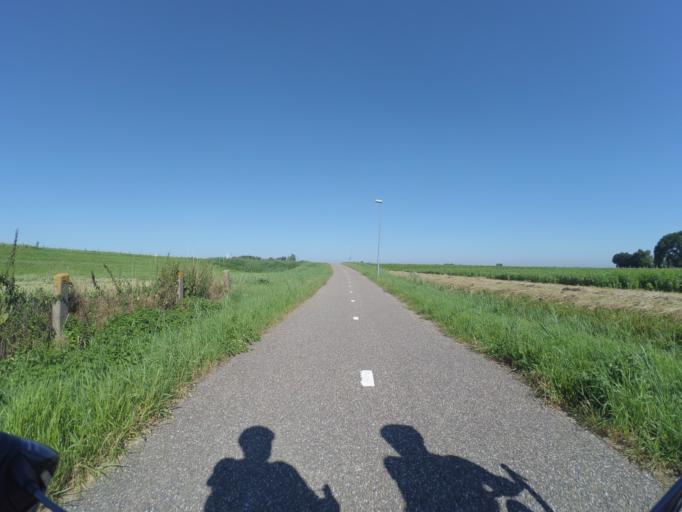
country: NL
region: North Brabant
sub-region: Gemeente Made en Drimmelen
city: Made
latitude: 51.6944
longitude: 4.7265
